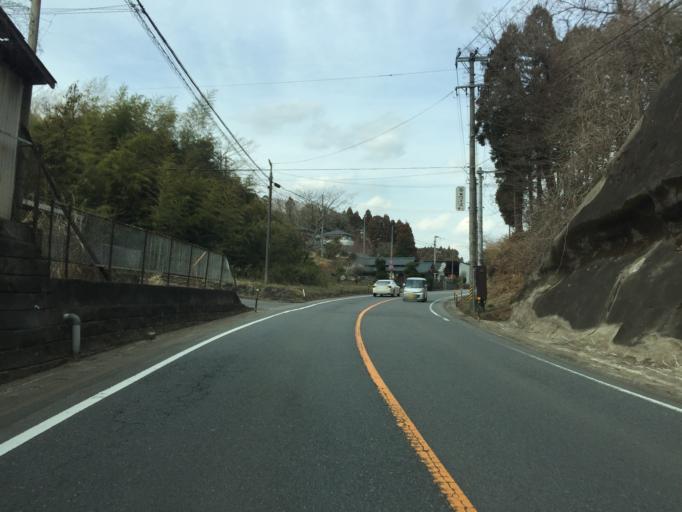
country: JP
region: Fukushima
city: Iwaki
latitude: 36.9757
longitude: 140.7389
